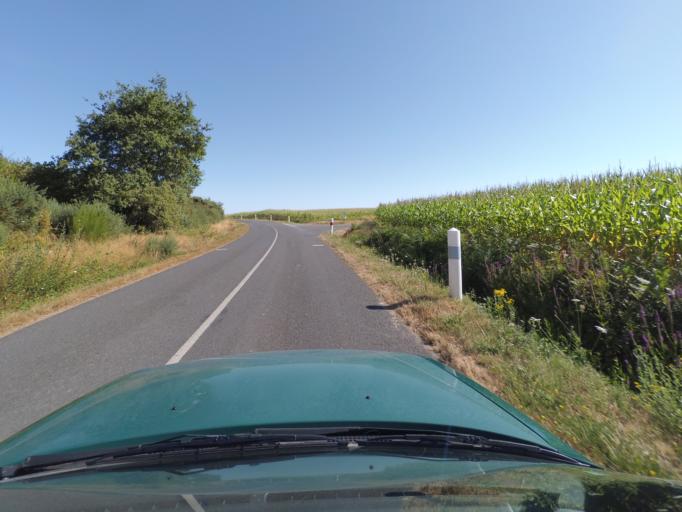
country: FR
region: Pays de la Loire
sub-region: Departement de la Loire-Atlantique
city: Maisdon-sur-Sevre
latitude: 47.0914
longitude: -1.3704
